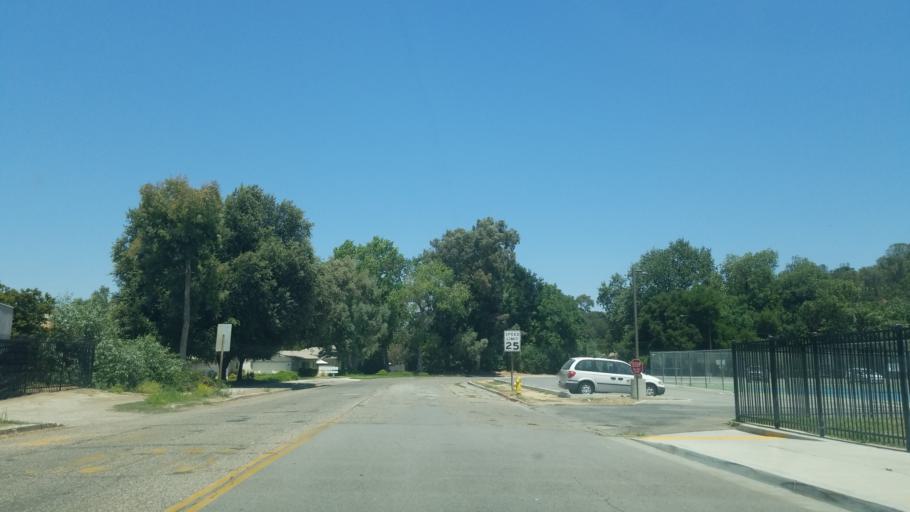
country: US
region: California
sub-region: San Luis Obispo County
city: Atascadero
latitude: 35.4920
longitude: -120.6662
